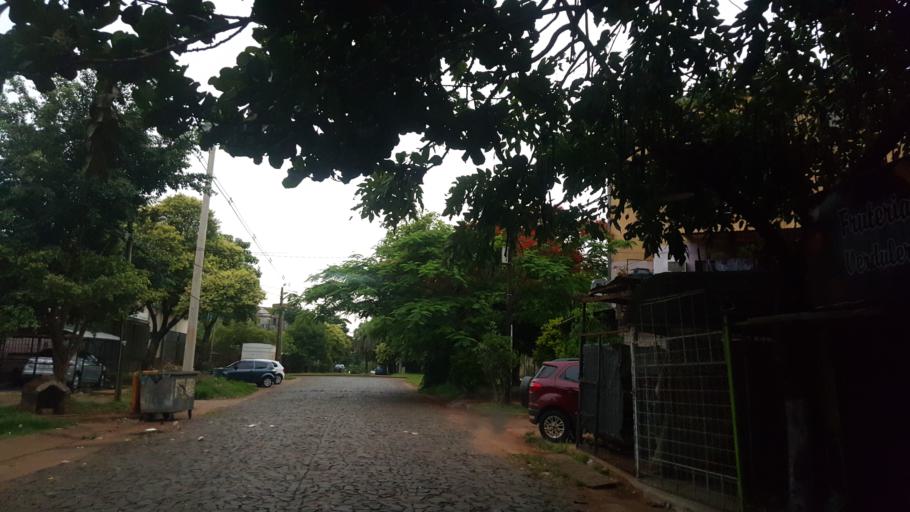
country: AR
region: Misiones
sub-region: Departamento de Capital
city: Posadas
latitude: -27.3580
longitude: -55.9313
